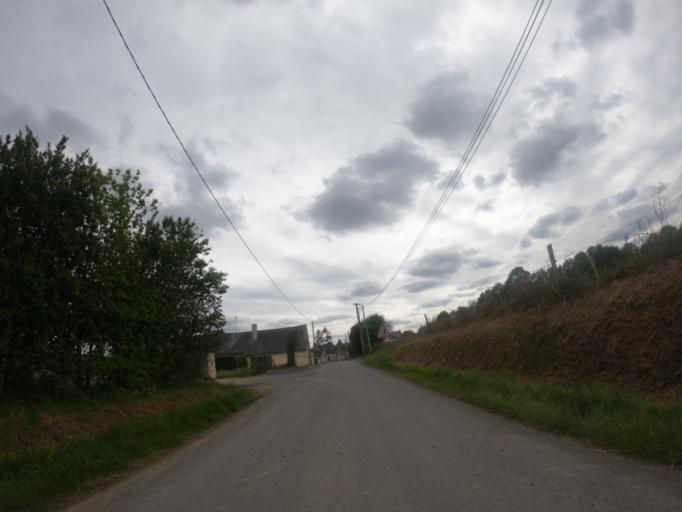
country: FR
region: Pays de la Loire
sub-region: Departement de la Loire-Atlantique
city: Chateaubriant
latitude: 47.7336
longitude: -1.4311
